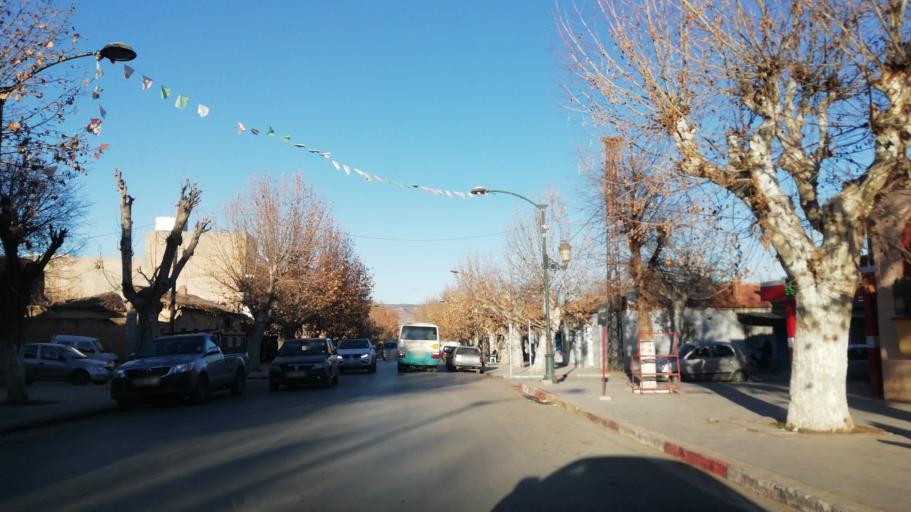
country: DZ
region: Tlemcen
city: Sebdou
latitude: 34.6396
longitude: -1.3302
